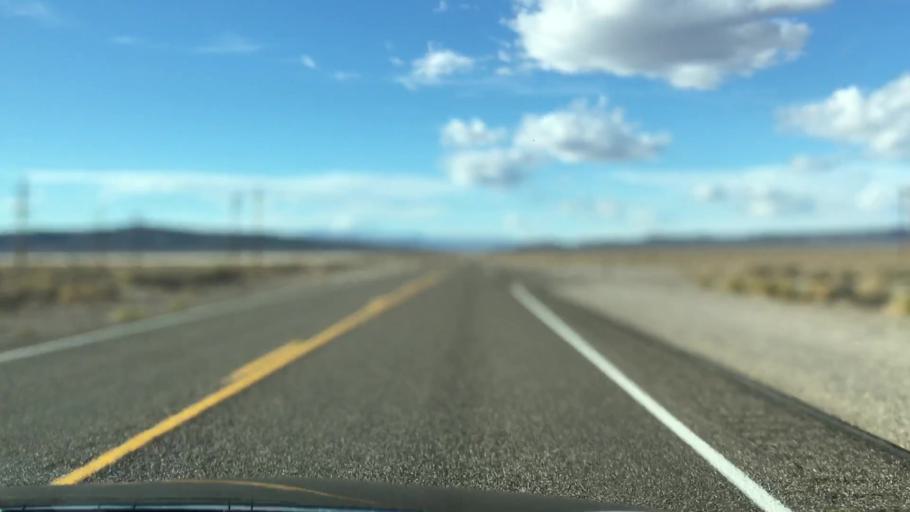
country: US
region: Nevada
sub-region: Nye County
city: Beatty
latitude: 37.1377
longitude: -116.8540
